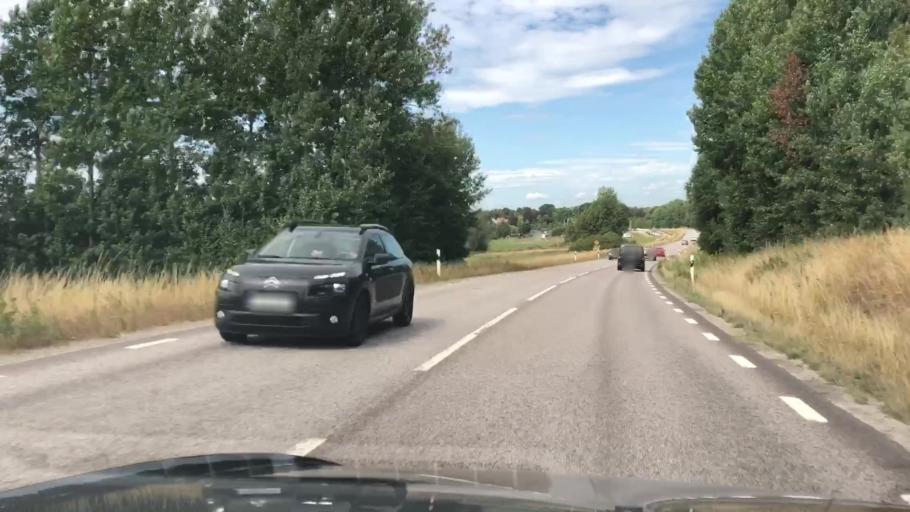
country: SE
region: Blekinge
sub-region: Karlskrona Kommun
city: Sturko
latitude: 56.1919
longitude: 15.7022
